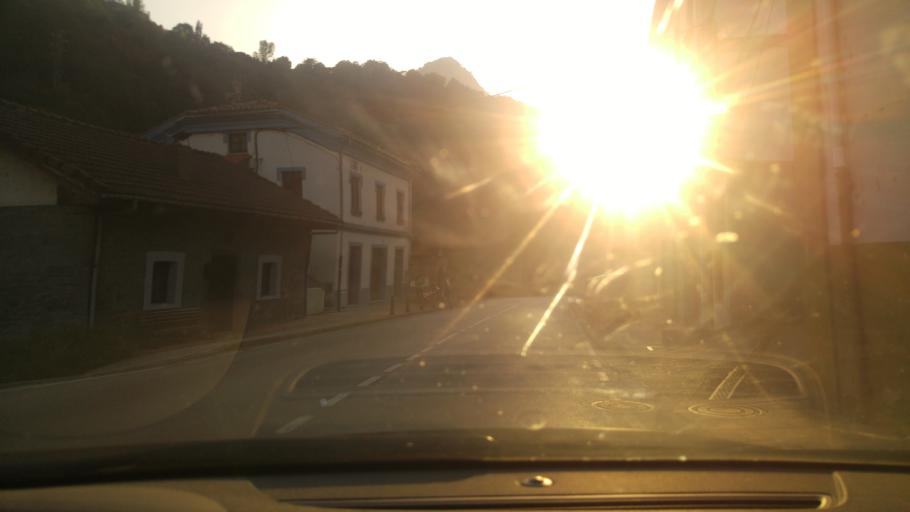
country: ES
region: Asturias
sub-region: Province of Asturias
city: Proaza
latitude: 43.2498
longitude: -6.0183
